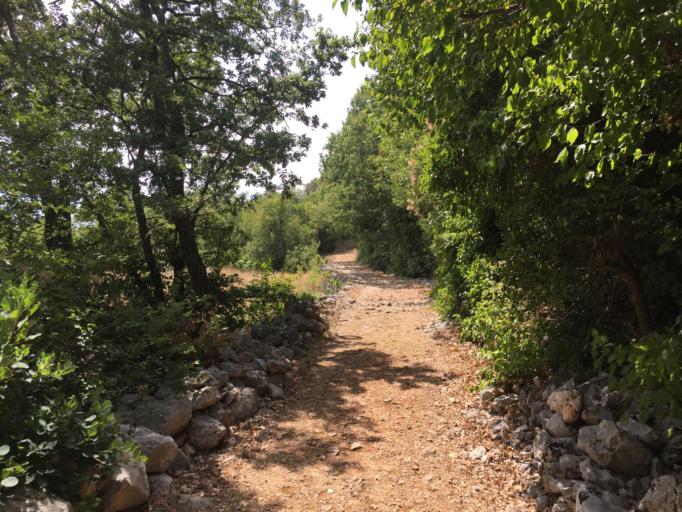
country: HR
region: Istarska
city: Lovran
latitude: 45.1812
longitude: 14.2385
